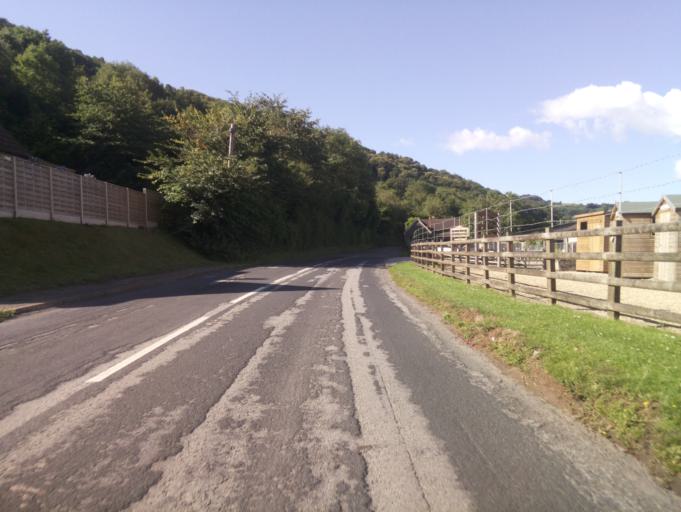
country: GB
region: England
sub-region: Herefordshire
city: Walford
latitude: 51.8759
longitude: -2.6016
